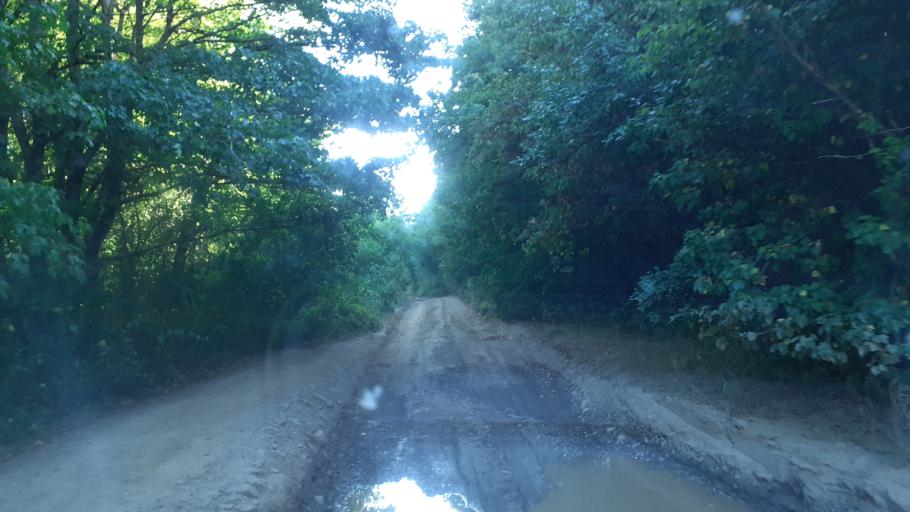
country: RU
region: Krasnodarskiy
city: Azovskaya
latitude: 44.6656
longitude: 38.4981
